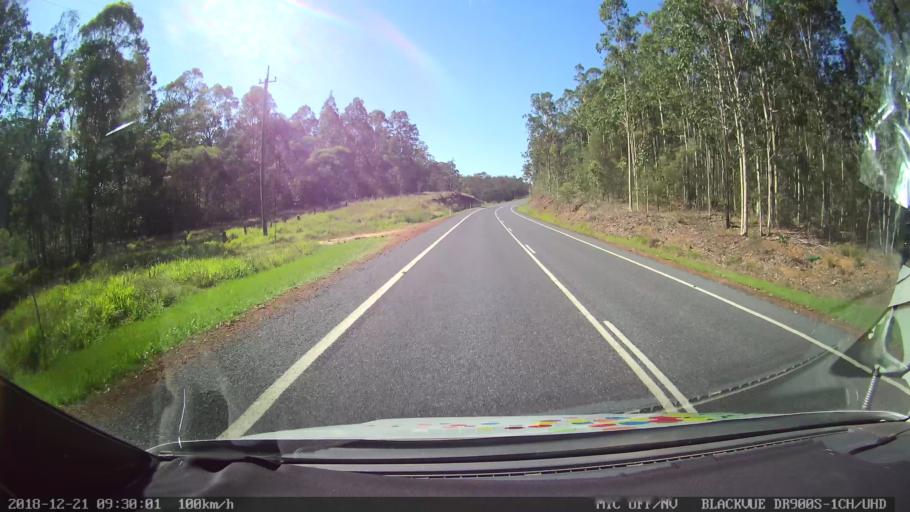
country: AU
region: New South Wales
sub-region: Clarence Valley
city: Maclean
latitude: -29.4404
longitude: 152.9913
